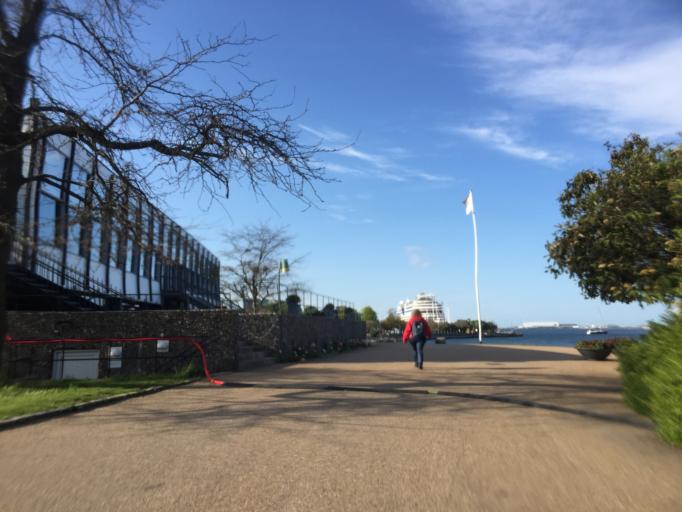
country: DK
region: Capital Region
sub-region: Kobenhavn
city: Christianshavn
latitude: 55.6911
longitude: 12.5988
